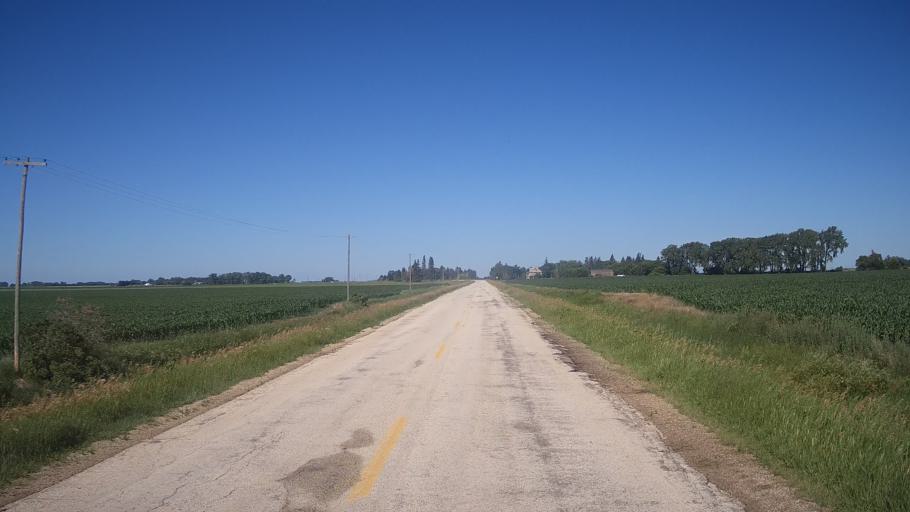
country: CA
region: Manitoba
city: Portage la Prairie
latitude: 50.0437
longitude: -98.0478
